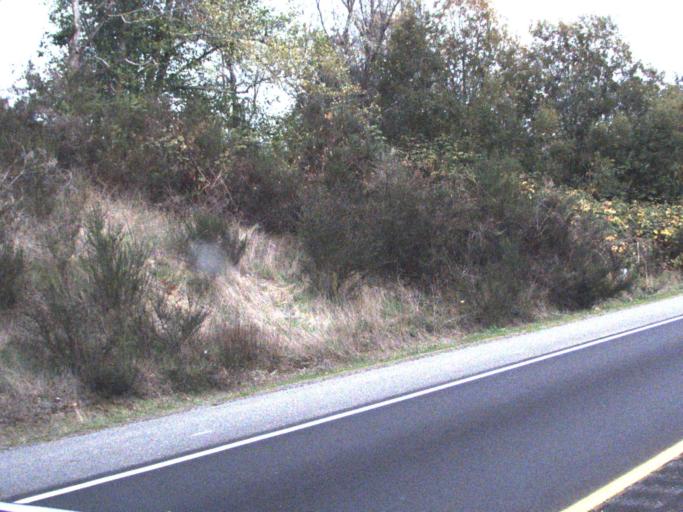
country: US
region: Washington
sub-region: Island County
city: Freeland
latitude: 48.0071
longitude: -122.4968
